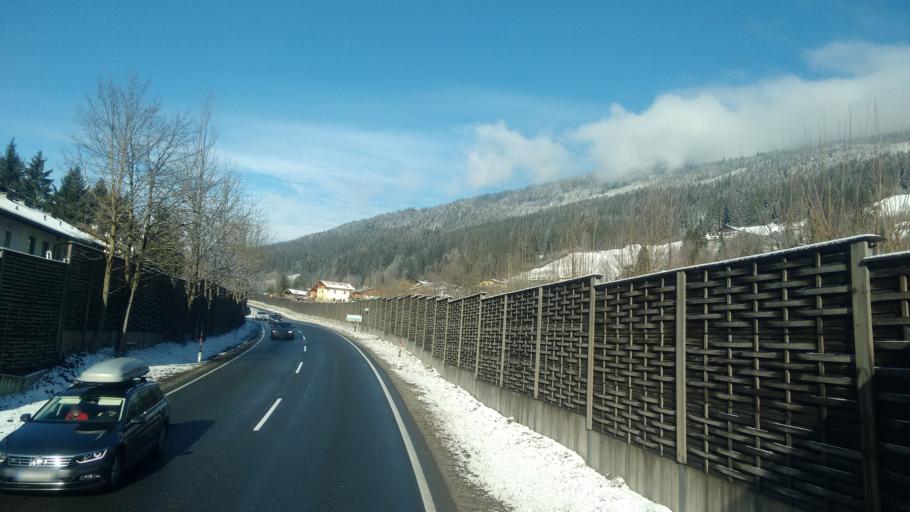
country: AT
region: Salzburg
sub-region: Politischer Bezirk Sankt Johann im Pongau
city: Radstadt
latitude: 47.3864
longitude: 13.4587
